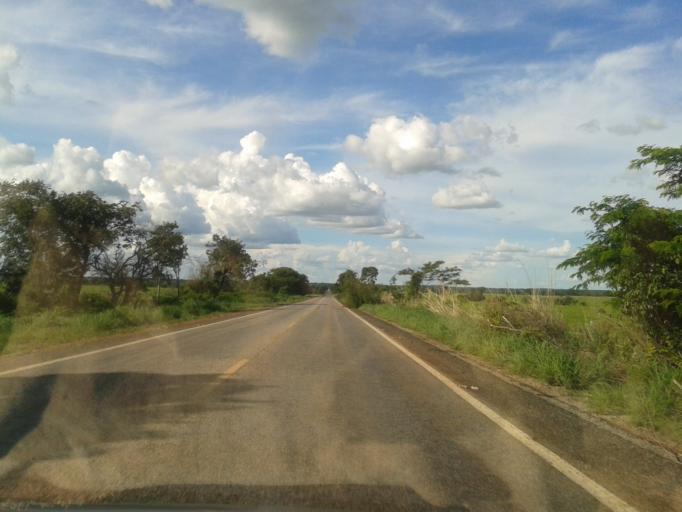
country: BR
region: Goias
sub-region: Mozarlandia
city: Mozarlandia
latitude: -14.5163
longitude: -50.4854
